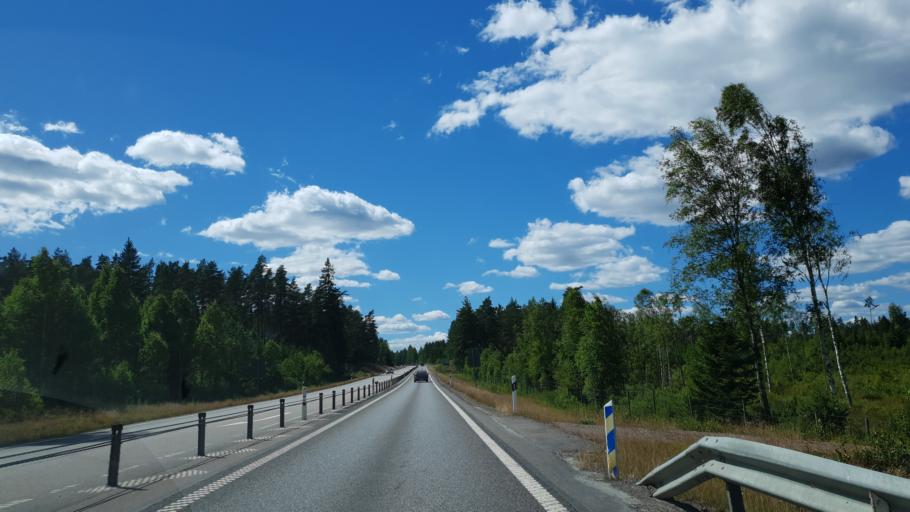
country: SE
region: Kronoberg
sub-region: Vaxjo Kommun
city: Ingelstad
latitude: 56.8697
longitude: 14.9976
